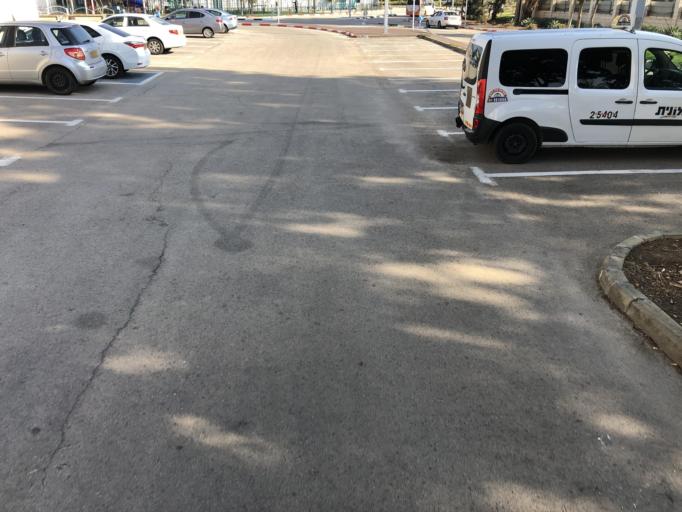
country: IL
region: Northern District
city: `Akko
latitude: 32.9176
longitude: 35.0913
